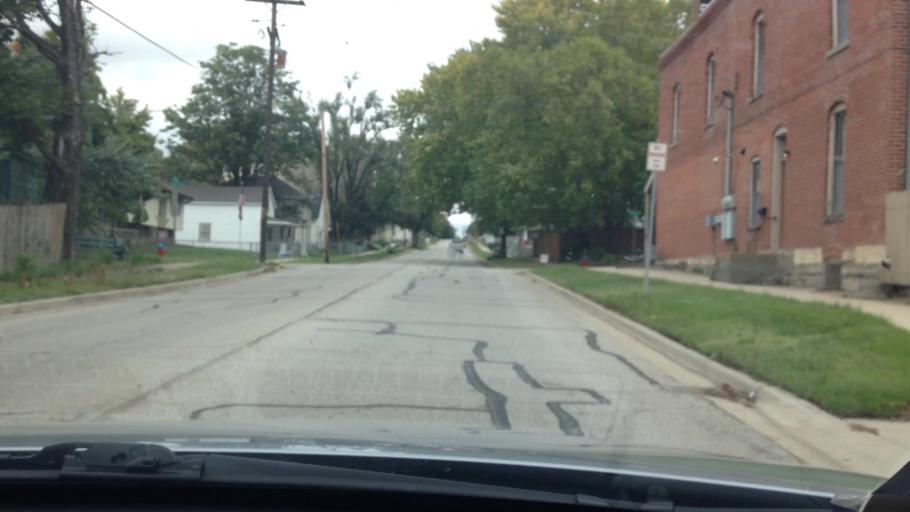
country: US
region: Kansas
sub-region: Leavenworth County
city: Leavenworth
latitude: 39.3201
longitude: -94.9283
